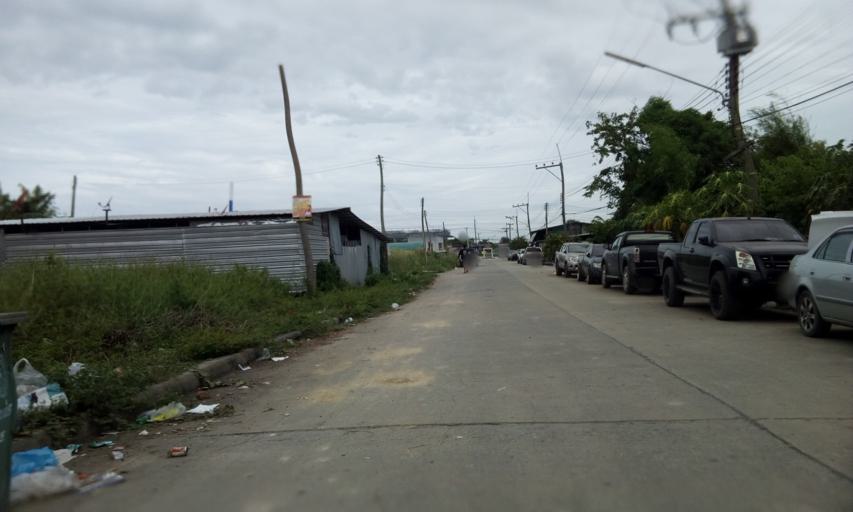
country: TH
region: Pathum Thani
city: Nong Suea
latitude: 14.0690
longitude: 100.8786
